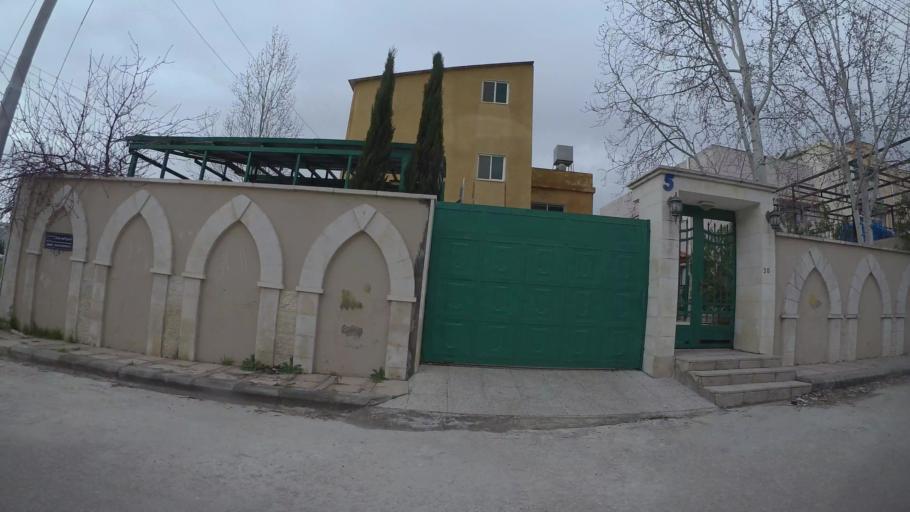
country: JO
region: Amman
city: Wadi as Sir
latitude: 31.9456
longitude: 35.8148
